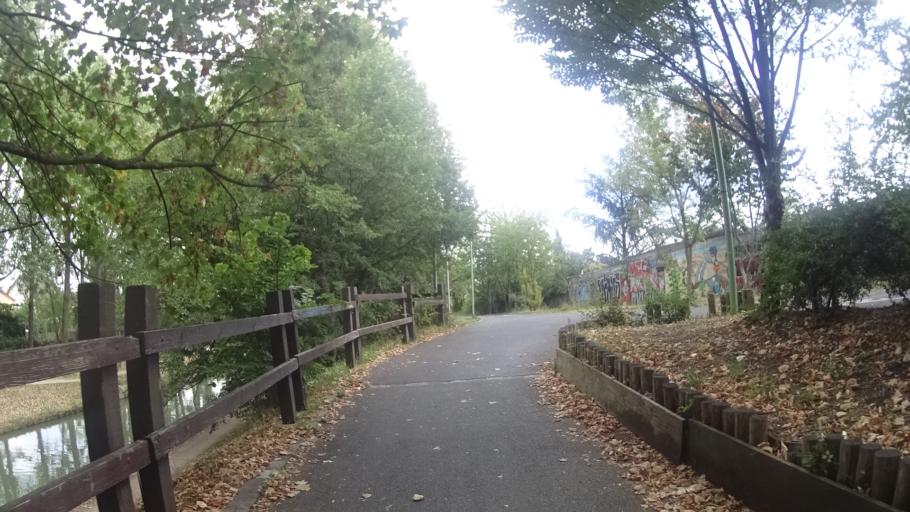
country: FR
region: Ile-de-France
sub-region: Departement de Seine-Saint-Denis
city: Les Pavillons-sous-Bois
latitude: 48.9249
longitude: 2.5138
